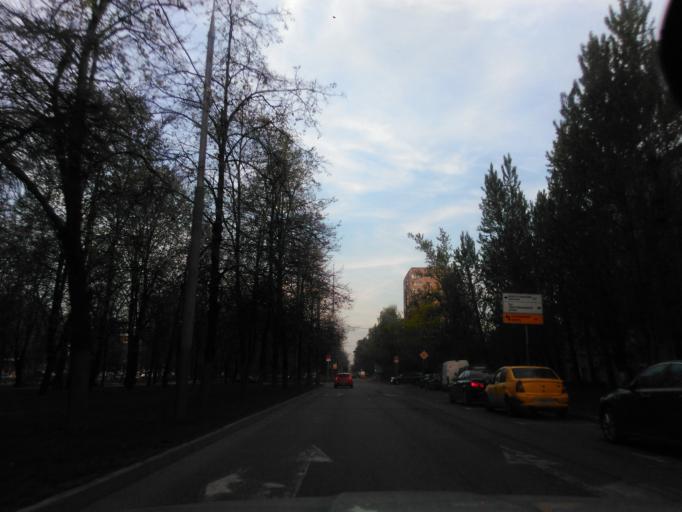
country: RU
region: Moscow
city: Novyye Kuz'minki
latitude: 55.7023
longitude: 37.7490
